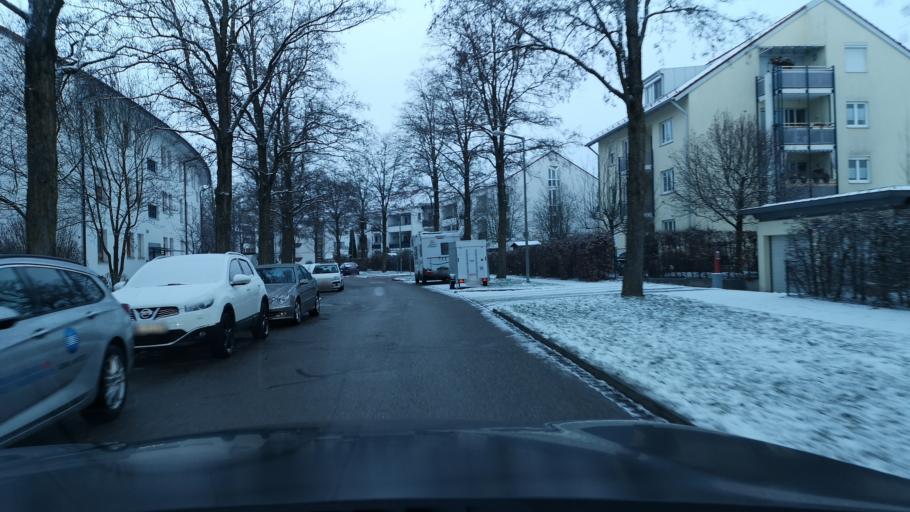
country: DE
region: Bavaria
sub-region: Upper Bavaria
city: Poing
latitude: 48.1749
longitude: 11.8034
